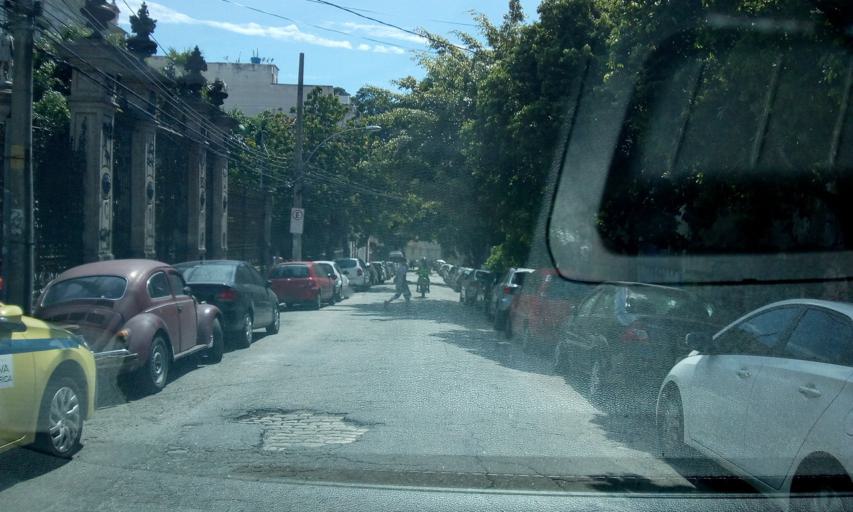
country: BR
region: Rio de Janeiro
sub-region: Rio De Janeiro
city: Rio de Janeiro
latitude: -22.9221
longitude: -43.1795
